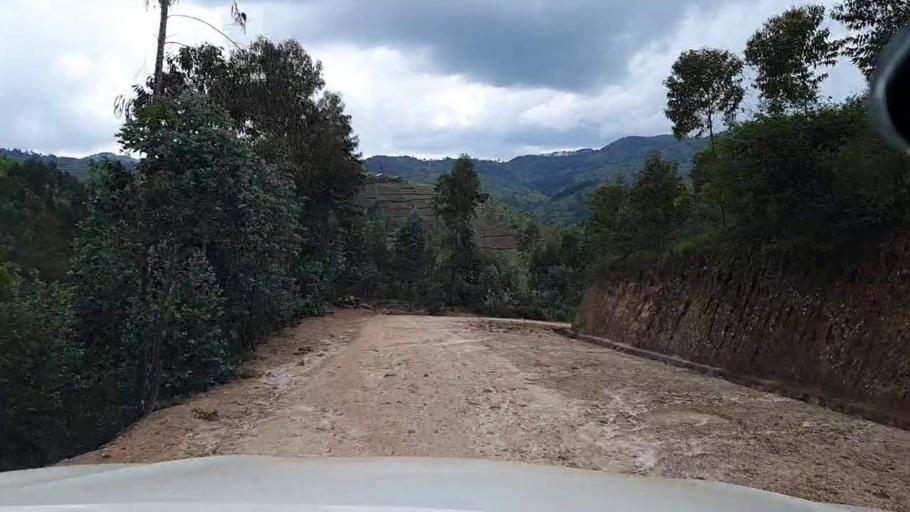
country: RW
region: Southern Province
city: Nzega
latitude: -2.6959
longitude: 29.4425
